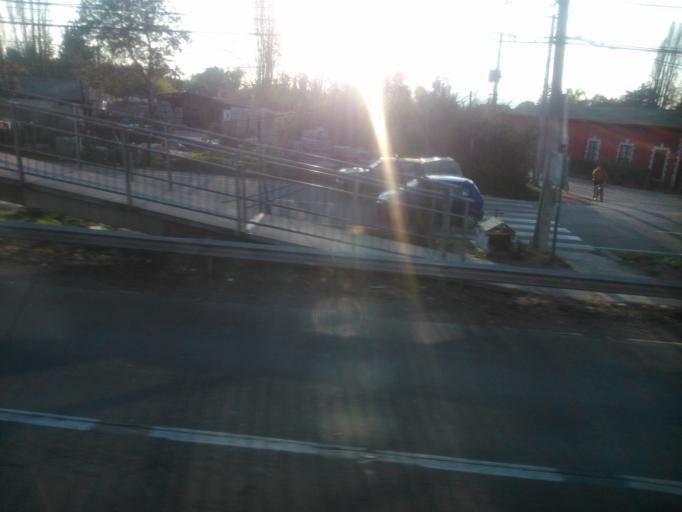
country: CL
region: Santiago Metropolitan
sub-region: Provincia de Maipo
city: Buin
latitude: -33.7432
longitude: -70.7382
